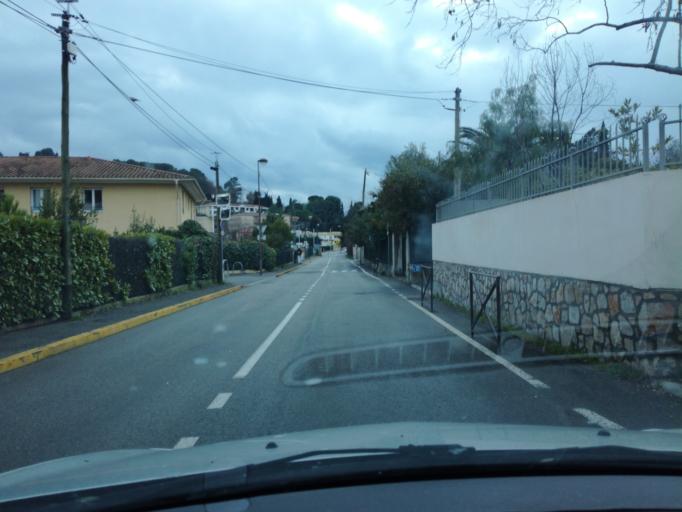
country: FR
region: Provence-Alpes-Cote d'Azur
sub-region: Departement des Alpes-Maritimes
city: Mougins
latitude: 43.6038
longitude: 6.9861
